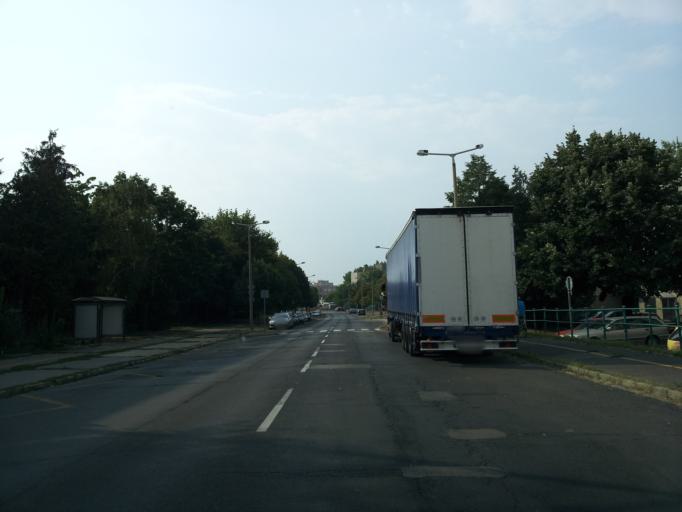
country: HU
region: Gyor-Moson-Sopron
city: Gyor
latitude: 47.6652
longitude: 17.6625
